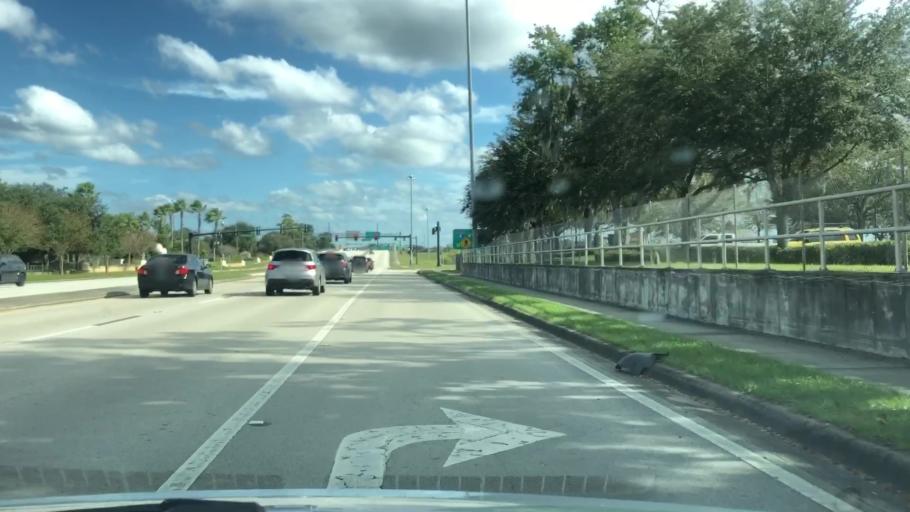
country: US
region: Florida
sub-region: Seminole County
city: Heathrow
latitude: 28.7863
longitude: -81.3557
